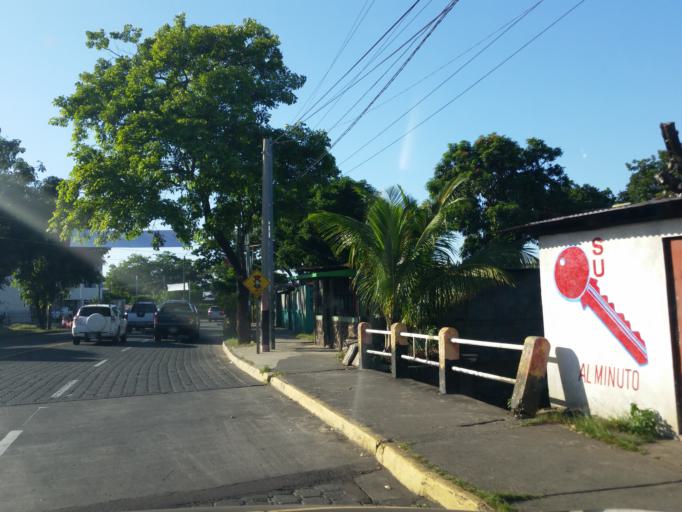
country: NI
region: Managua
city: Managua
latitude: 12.1385
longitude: -86.2925
